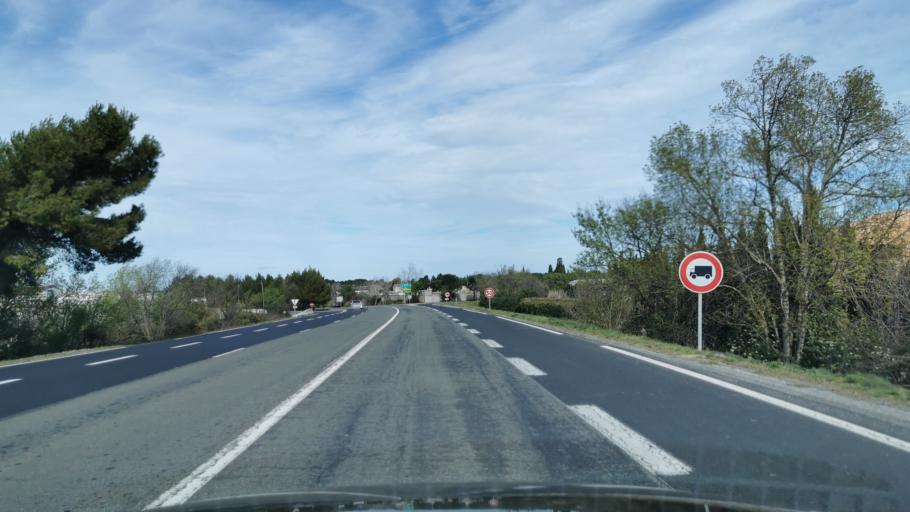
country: FR
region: Languedoc-Roussillon
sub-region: Departement de l'Aude
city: Sigean
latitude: 43.0282
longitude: 2.9667
